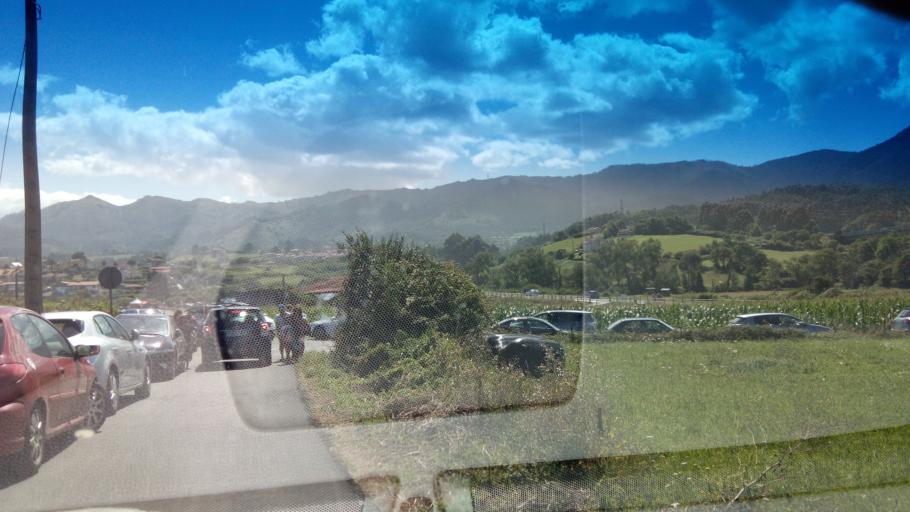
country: ES
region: Asturias
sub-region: Province of Asturias
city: Colunga
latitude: 43.4751
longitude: -5.2184
